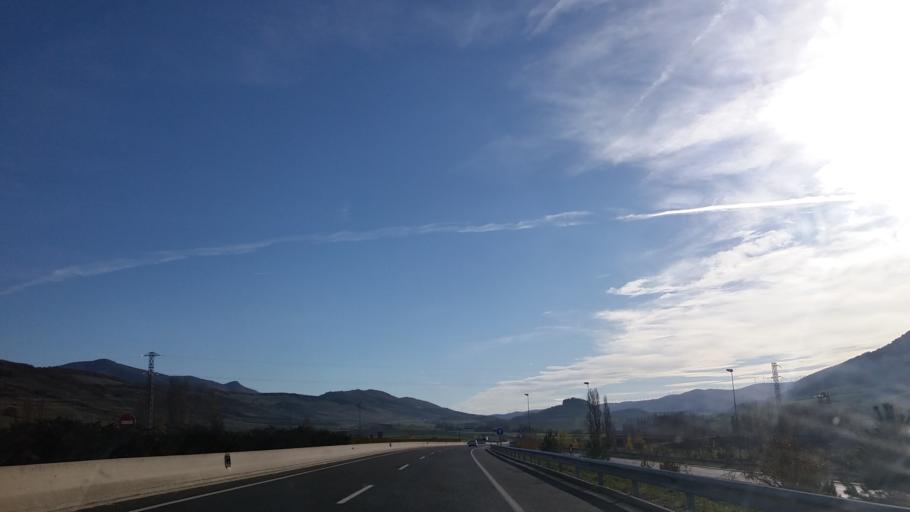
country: ES
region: Navarre
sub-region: Provincia de Navarra
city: Elorz
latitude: 42.7198
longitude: -1.5348
